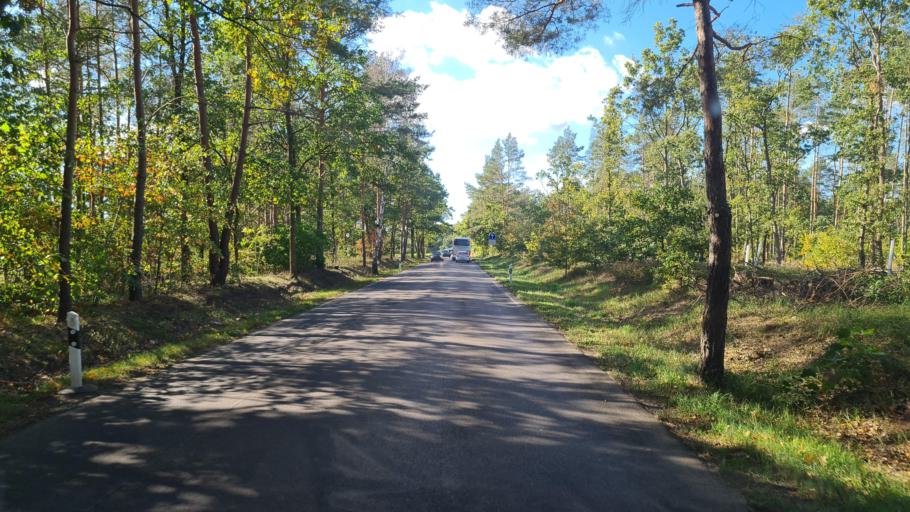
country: DE
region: Brandenburg
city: Kolkwitz
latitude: 51.7634
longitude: 14.2748
